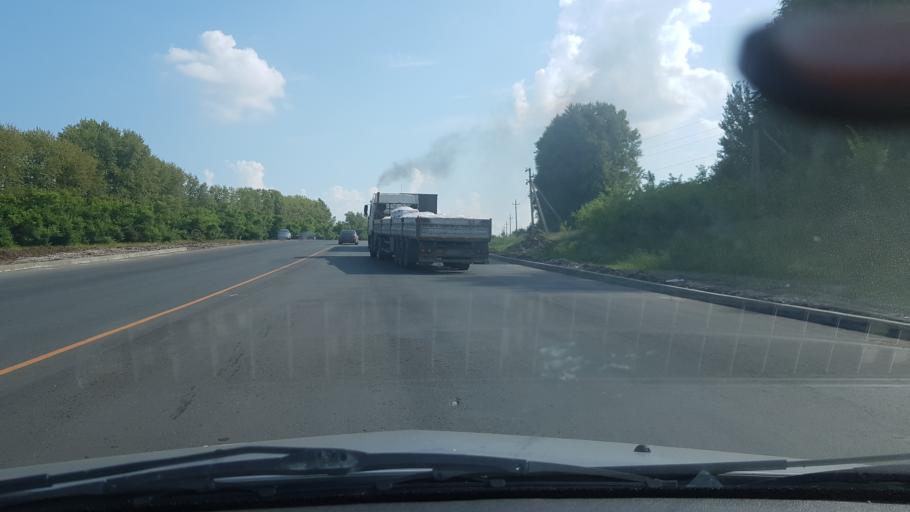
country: RU
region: Chuvashia
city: Tsivil'sk
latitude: 55.7306
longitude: 47.4479
